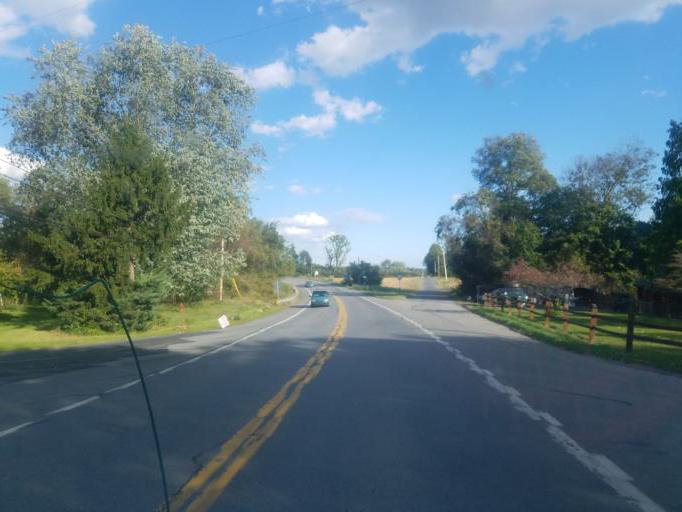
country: US
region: Pennsylvania
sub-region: Lancaster County
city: Maytown
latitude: 40.0653
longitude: -76.6112
